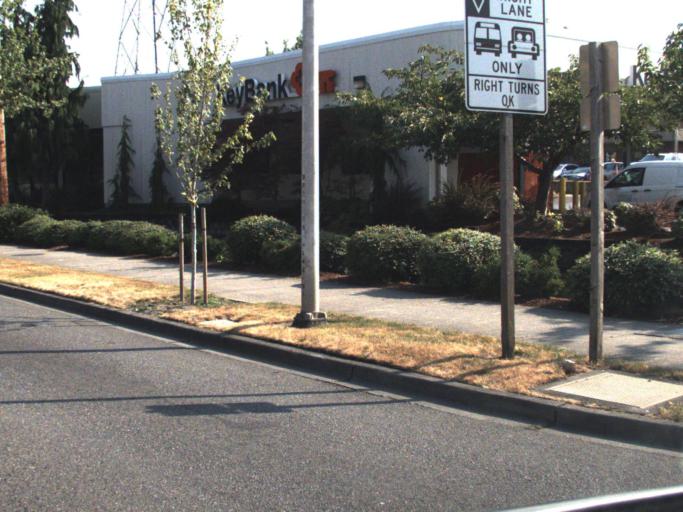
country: US
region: Washington
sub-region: King County
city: Federal Way
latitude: 47.3109
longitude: -122.3133
